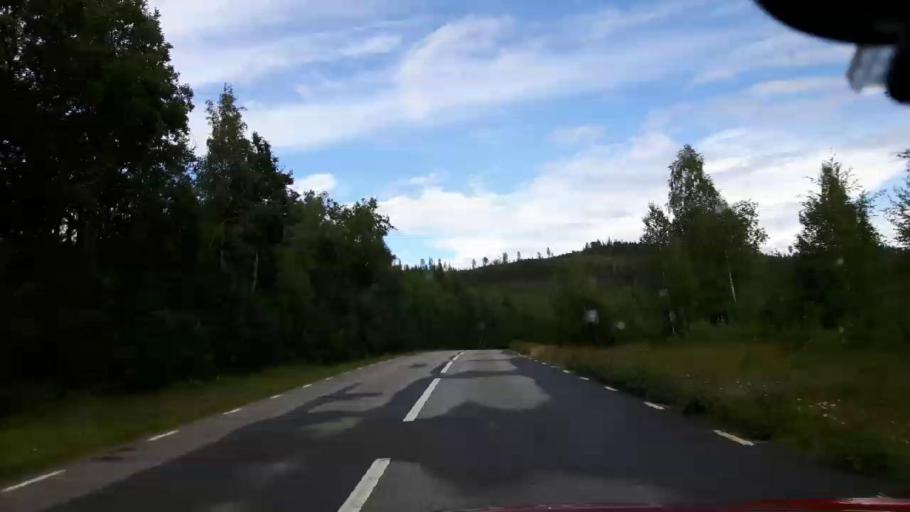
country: SE
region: Jaemtland
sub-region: Stroemsunds Kommun
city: Stroemsund
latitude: 64.3433
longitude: 15.0415
